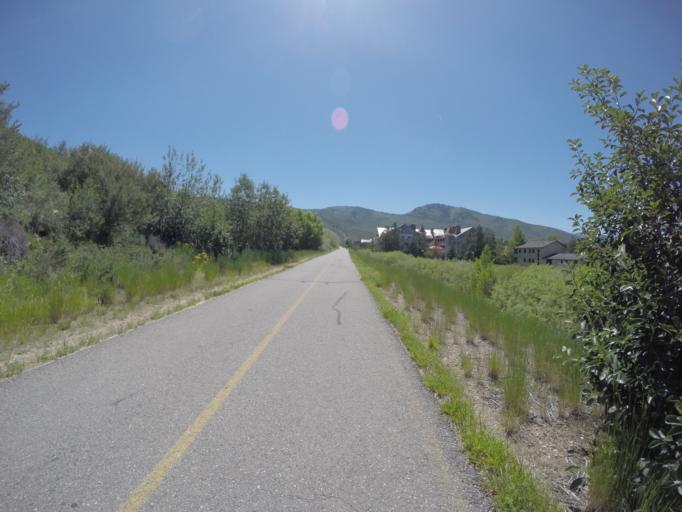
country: US
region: Utah
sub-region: Summit County
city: Park City
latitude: 40.6621
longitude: -111.4957
